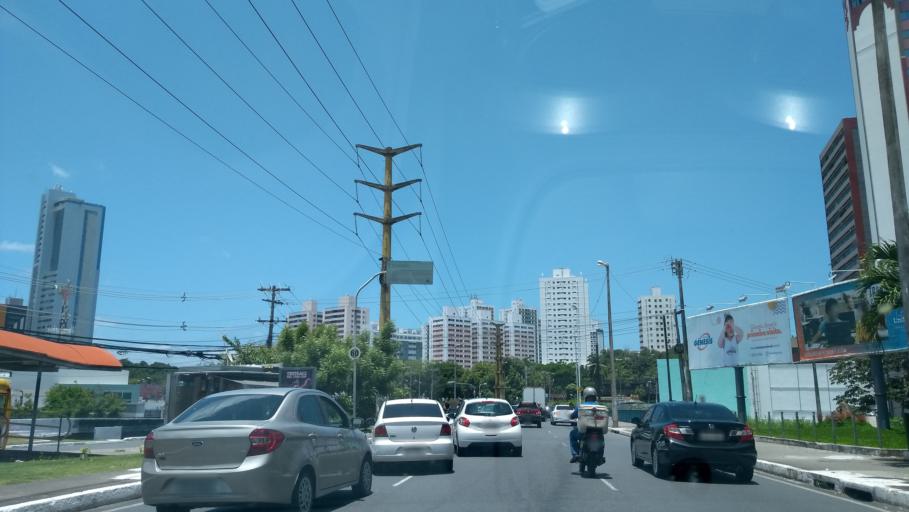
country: BR
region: Bahia
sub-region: Salvador
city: Salvador
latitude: -12.9843
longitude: -38.4517
